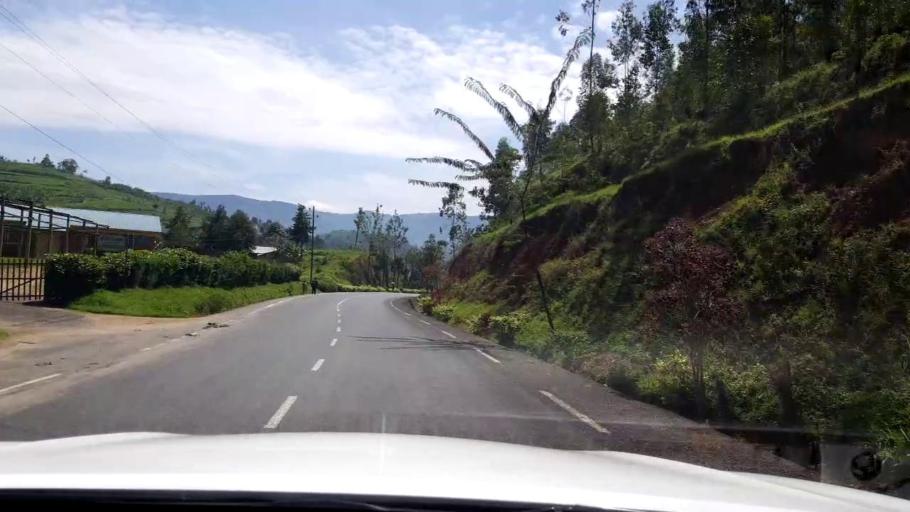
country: RW
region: Southern Province
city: Gitarama
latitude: -1.9217
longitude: 29.6502
